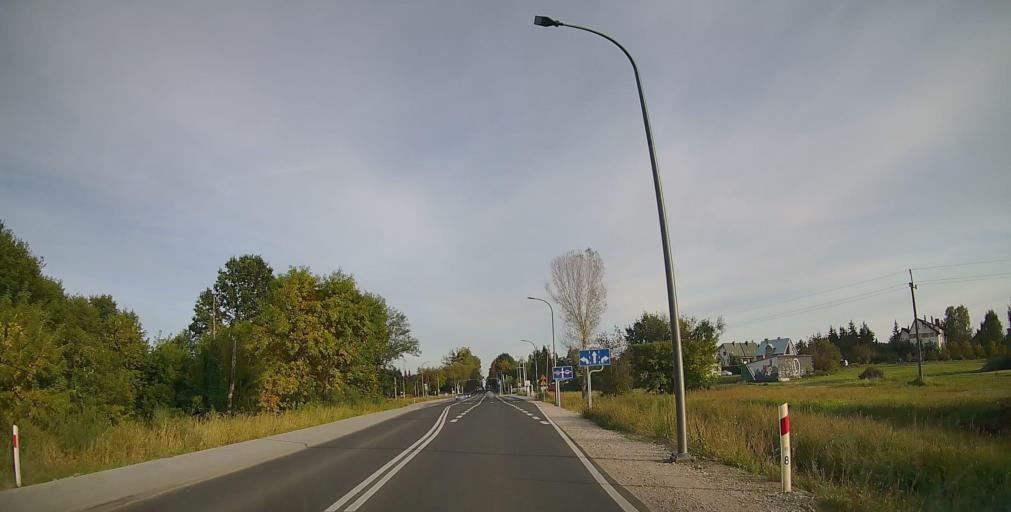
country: PL
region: Masovian Voivodeship
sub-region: Powiat piaseczynski
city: Zabieniec
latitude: 52.0596
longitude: 21.0455
